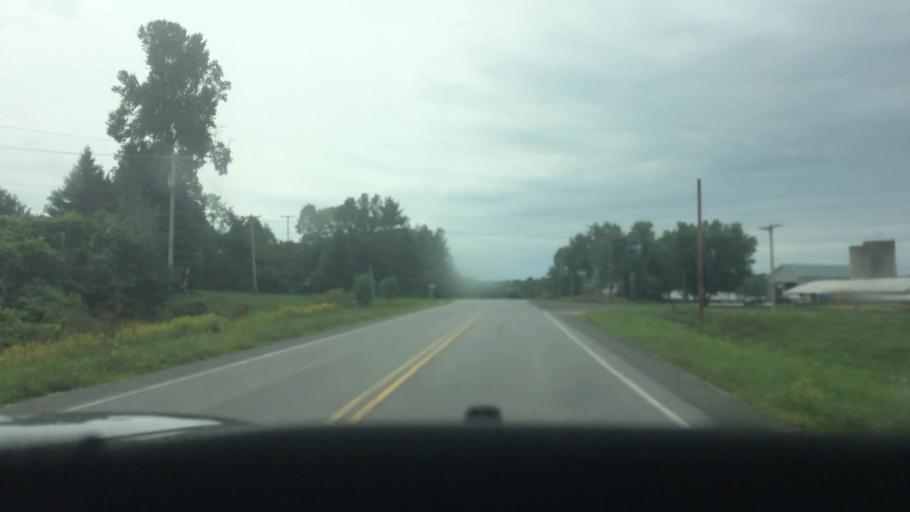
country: US
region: New York
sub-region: St. Lawrence County
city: Canton
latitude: 44.4893
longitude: -75.2490
